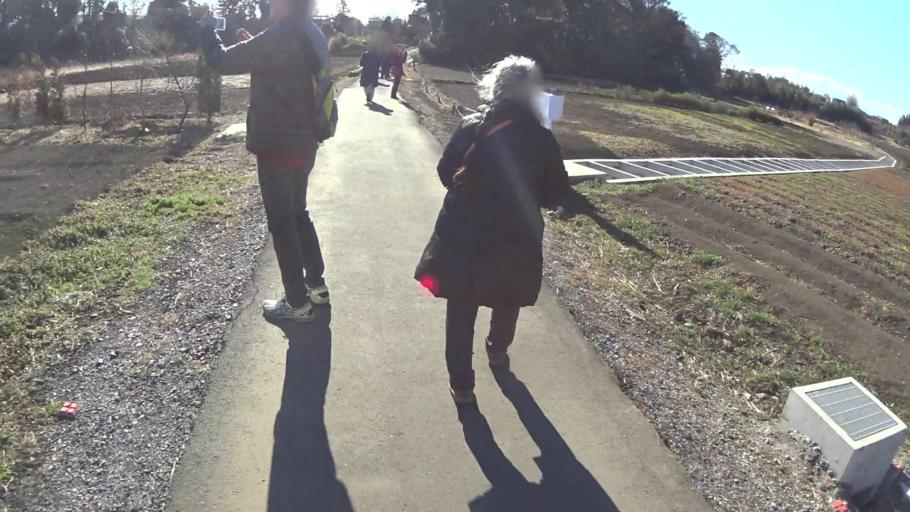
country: JP
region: Saitama
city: Saitama
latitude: 35.8954
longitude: 139.7170
